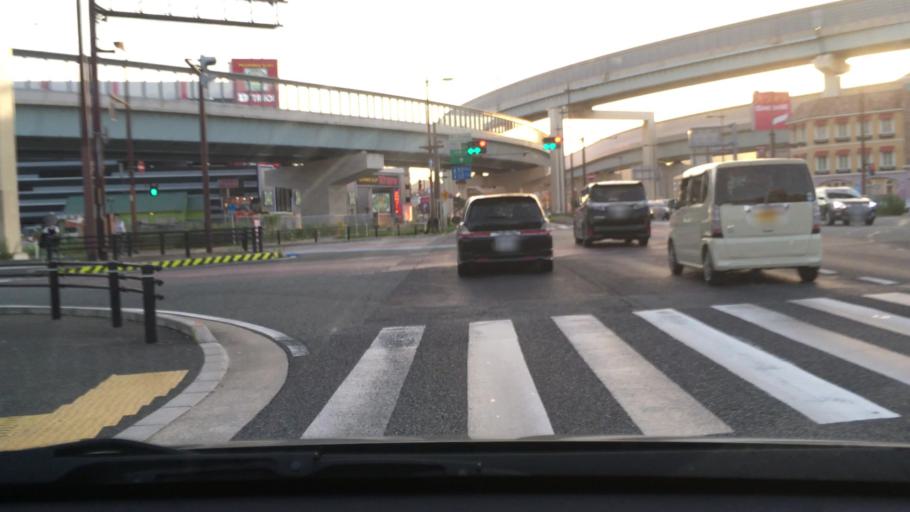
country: JP
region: Fukuoka
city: Fukuoka-shi
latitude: 33.5683
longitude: 130.3178
